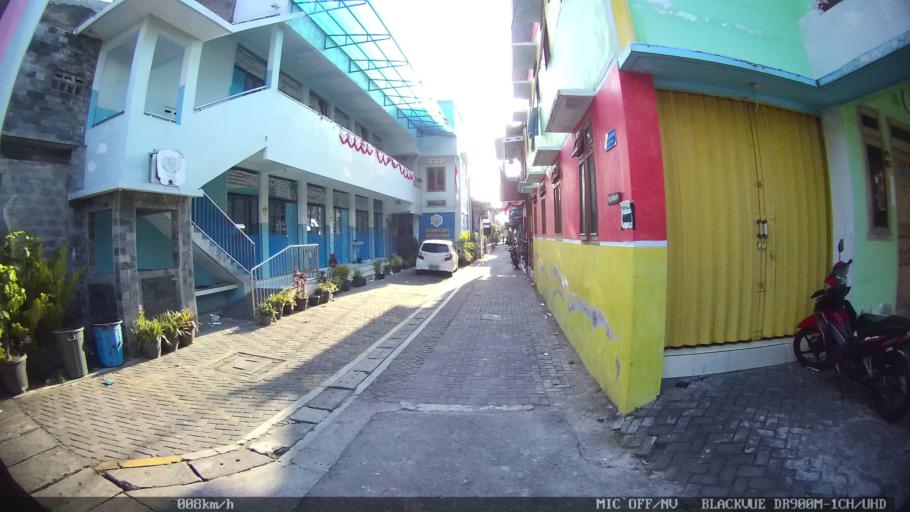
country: ID
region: Daerah Istimewa Yogyakarta
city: Yogyakarta
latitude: -7.8228
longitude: 110.3886
